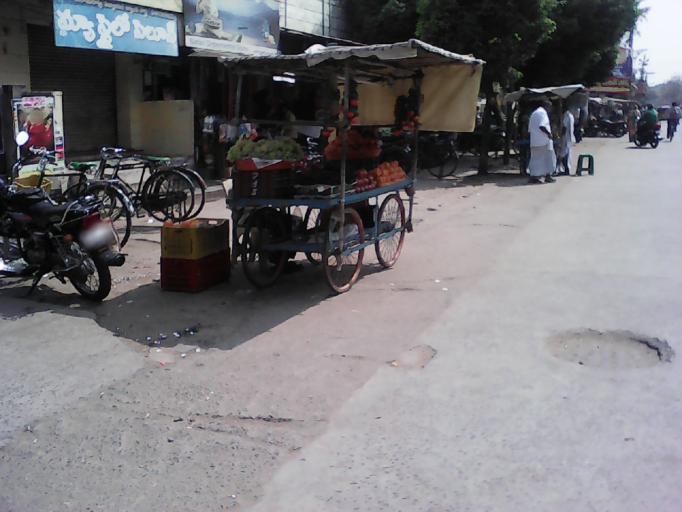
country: IN
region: Andhra Pradesh
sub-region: Guntur
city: Bhattiprolu
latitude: 16.2340
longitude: 80.6504
